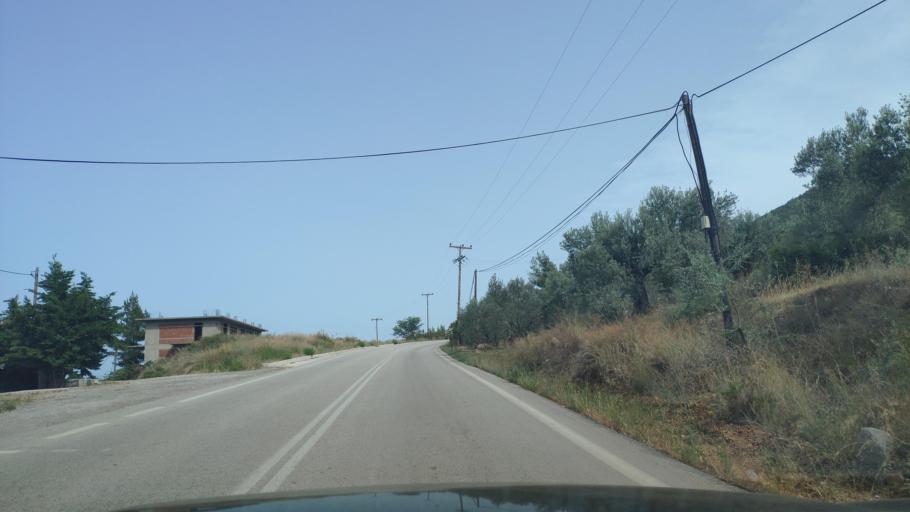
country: GR
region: Peloponnese
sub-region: Nomos Argolidos
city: Palaia Epidavros
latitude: 37.6309
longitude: 23.1390
